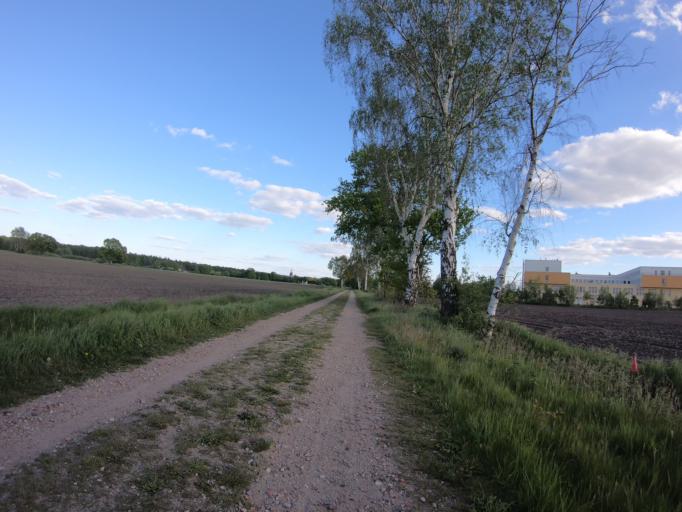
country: DE
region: Lower Saxony
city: Gifhorn
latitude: 52.4988
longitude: 10.5492
